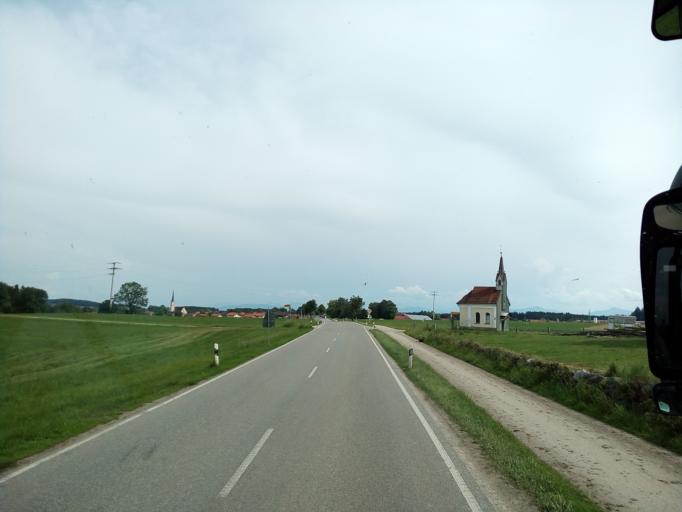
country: DE
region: Bavaria
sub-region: Upper Bavaria
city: Obing
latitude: 48.0071
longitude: 12.3936
